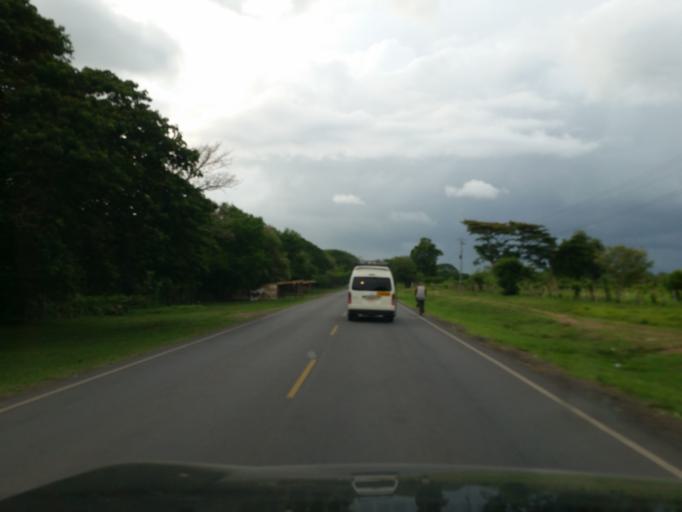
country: NI
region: Granada
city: Nandaime
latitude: 11.7368
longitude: -86.0198
